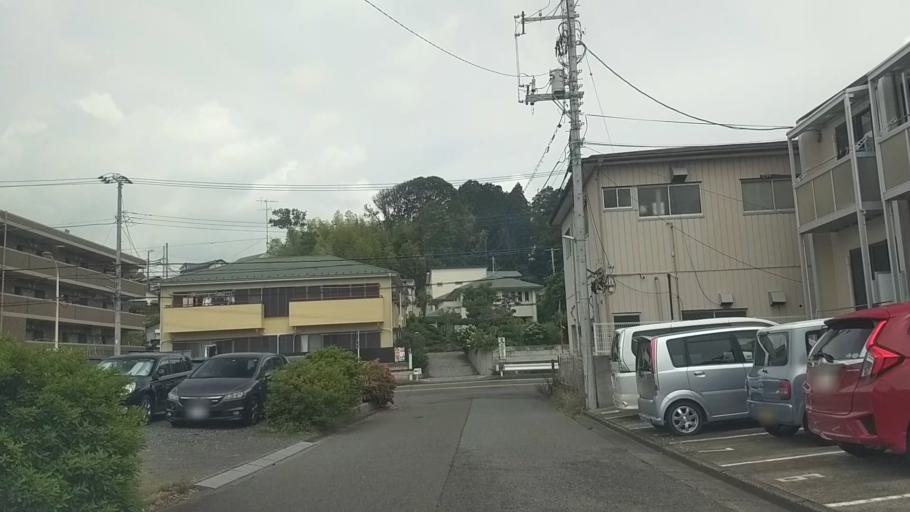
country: JP
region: Kanagawa
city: Fujisawa
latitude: 35.3633
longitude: 139.4692
